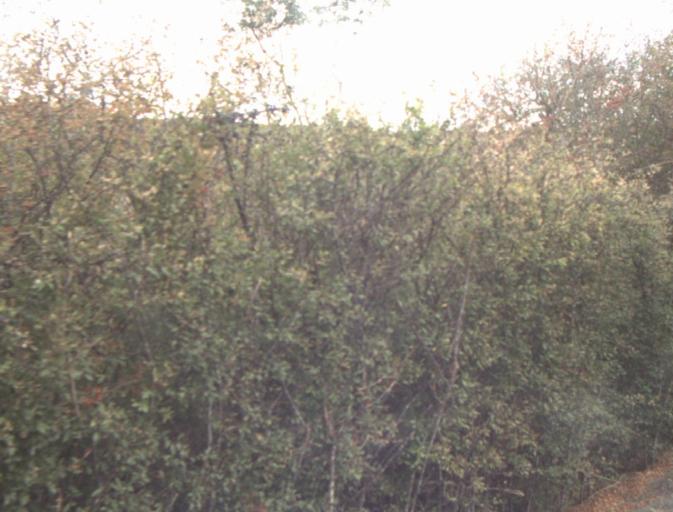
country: AU
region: Tasmania
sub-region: Northern Midlands
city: Evandale
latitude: -41.5292
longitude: 147.2442
